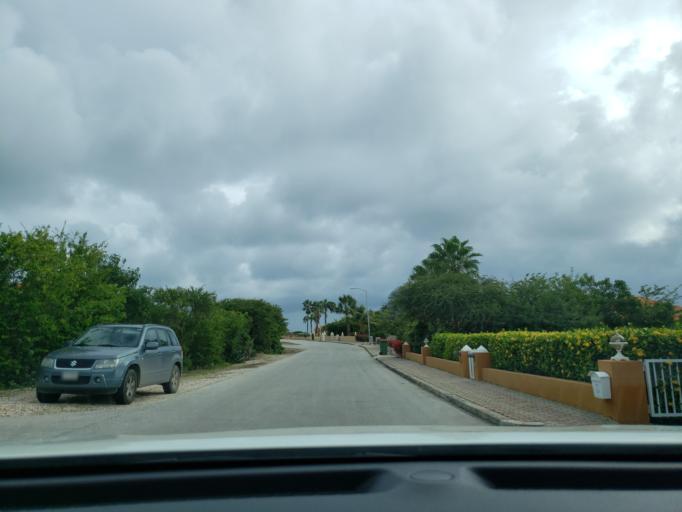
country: CW
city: Dorp Soto
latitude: 12.1985
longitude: -69.0764
